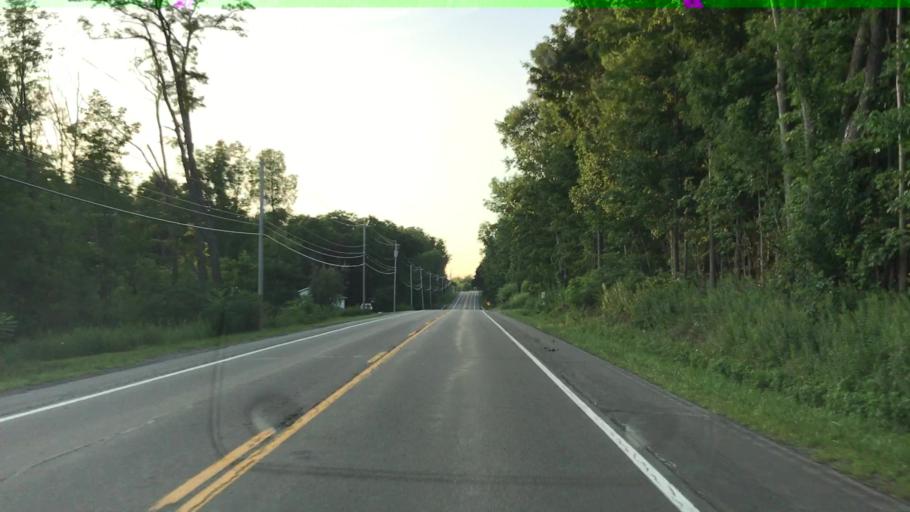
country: US
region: New York
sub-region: Chautauqua County
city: Mayville
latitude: 42.2541
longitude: -79.4661
